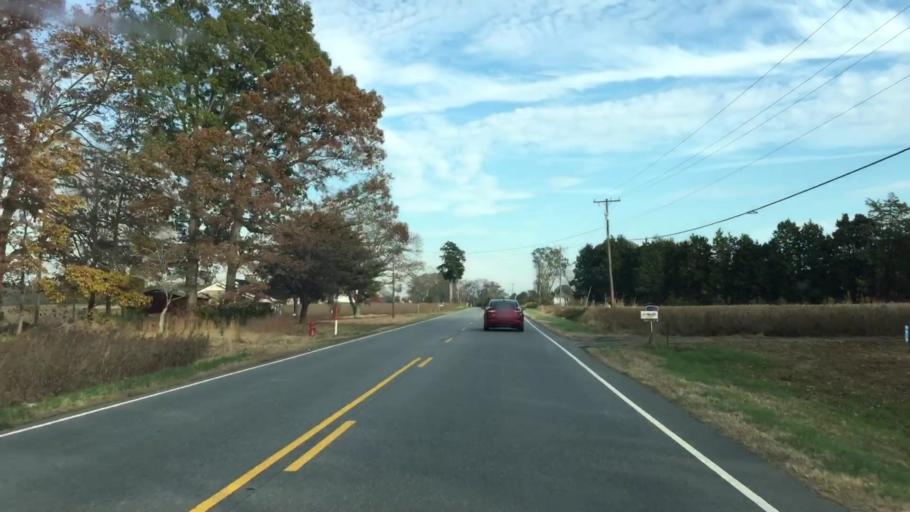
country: US
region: North Carolina
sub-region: Rockingham County
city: Reidsville
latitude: 36.2888
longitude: -79.7433
